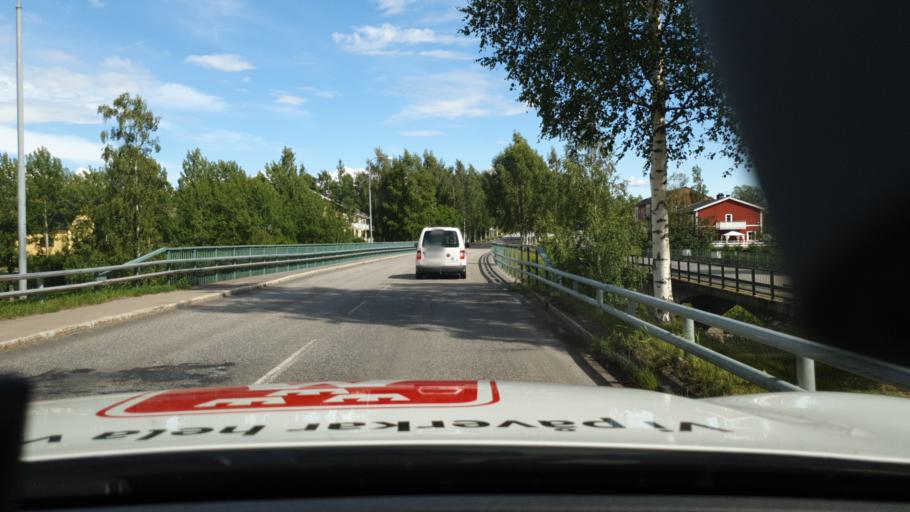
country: SE
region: Norrbotten
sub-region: Lulea Kommun
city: Ranea
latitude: 65.8548
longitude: 22.2816
